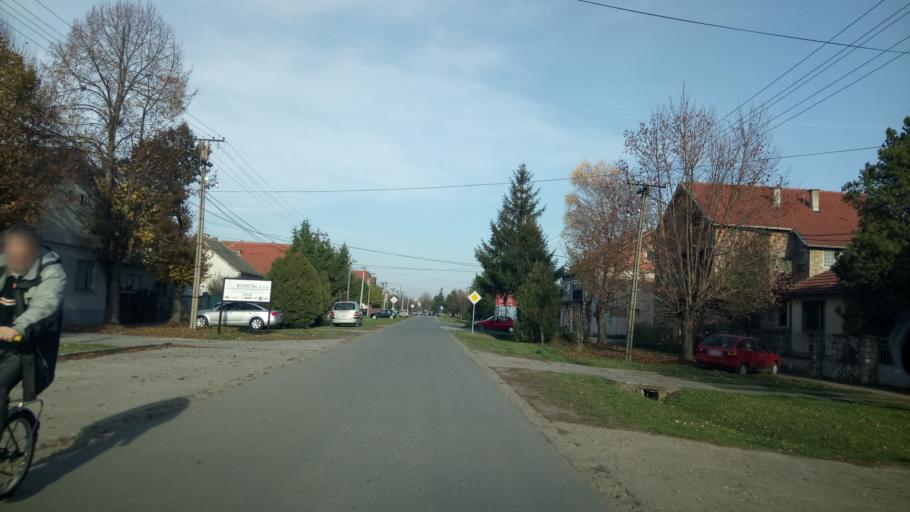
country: RS
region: Autonomna Pokrajina Vojvodina
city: Nova Pazova
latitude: 44.9492
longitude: 20.2252
